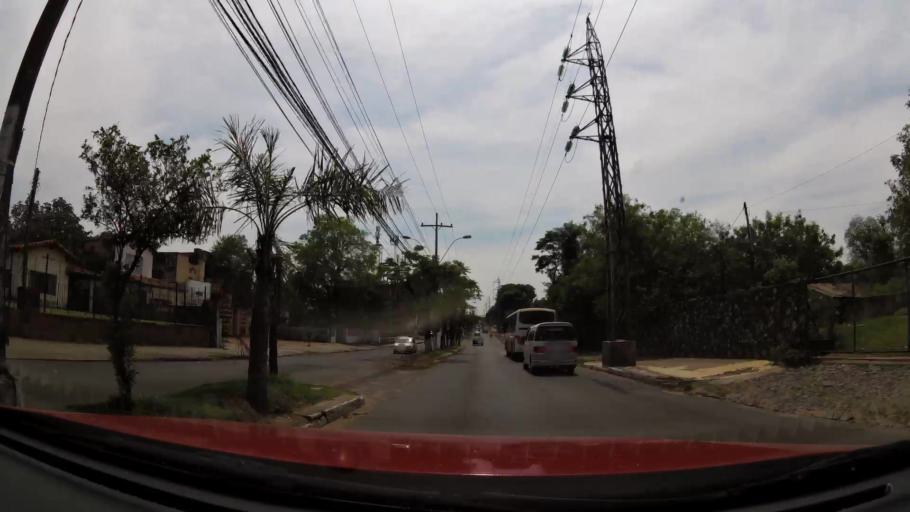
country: PY
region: Asuncion
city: Asuncion
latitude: -25.2630
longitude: -57.5929
